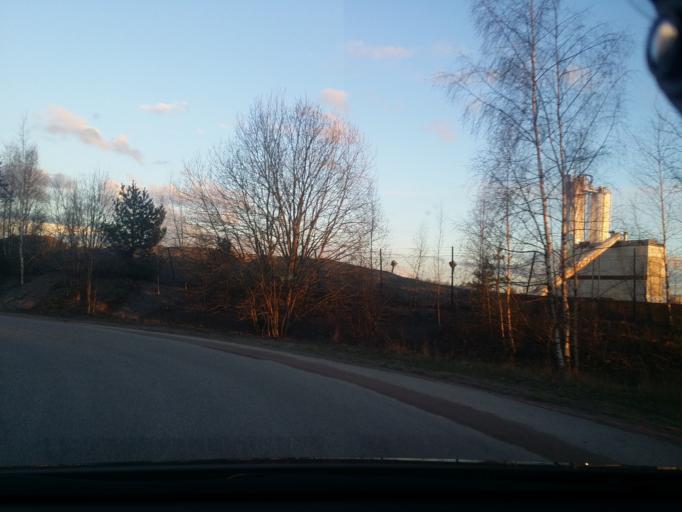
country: SE
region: Vaestmanland
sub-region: Vasteras
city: Vasteras
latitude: 59.6357
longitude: 16.5747
